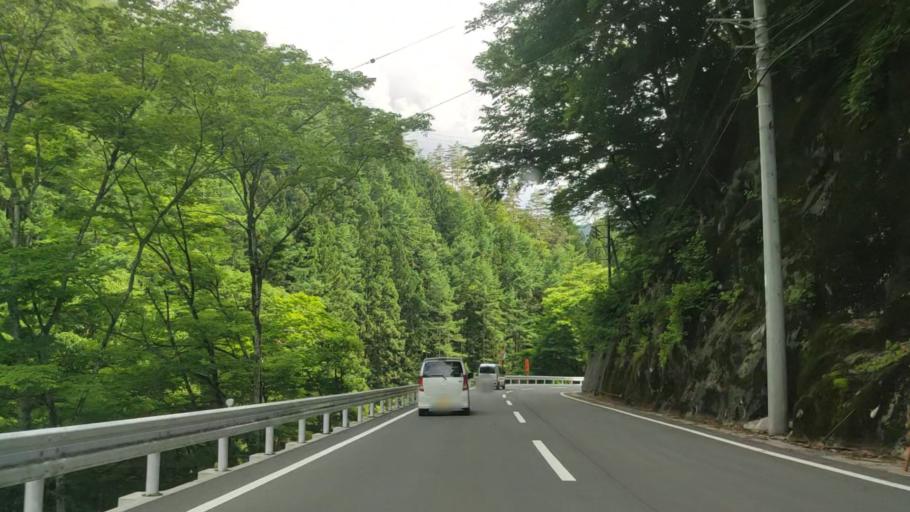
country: JP
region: Gunma
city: Tomioka
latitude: 36.0999
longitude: 138.7181
